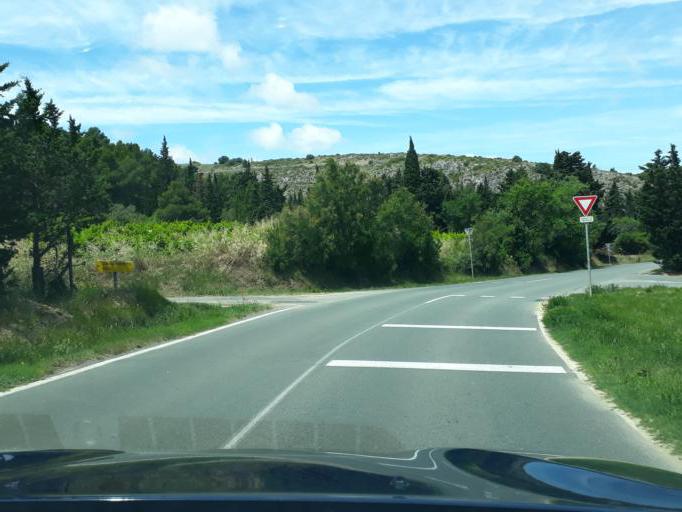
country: FR
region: Languedoc-Roussillon
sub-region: Departement de l'Aude
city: Portel-des-Corbieres
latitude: 43.0473
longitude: 2.9251
